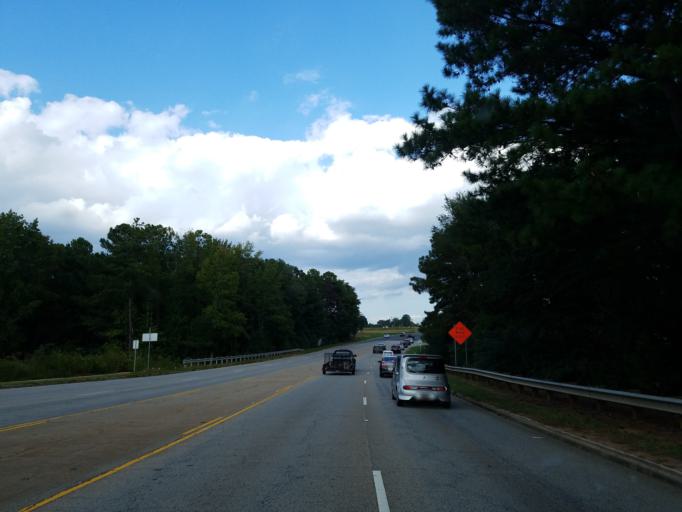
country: US
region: South Carolina
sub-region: Greenville County
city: Mauldin
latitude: 34.8257
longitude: -82.3274
